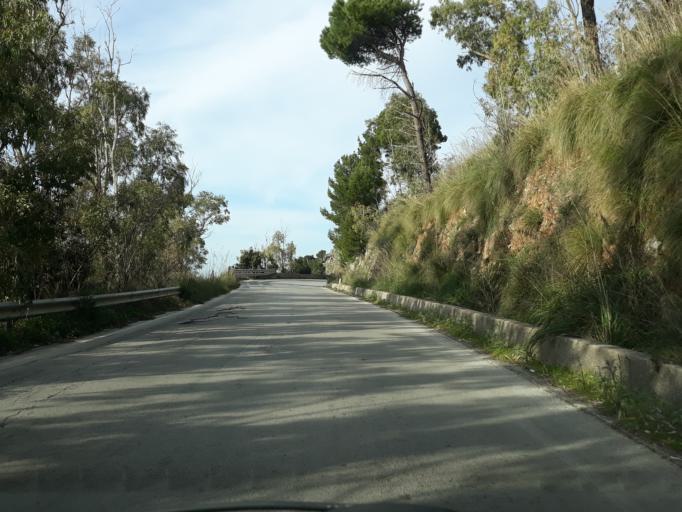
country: IT
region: Sicily
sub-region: Palermo
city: Torretta
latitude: 38.1155
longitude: 13.2421
